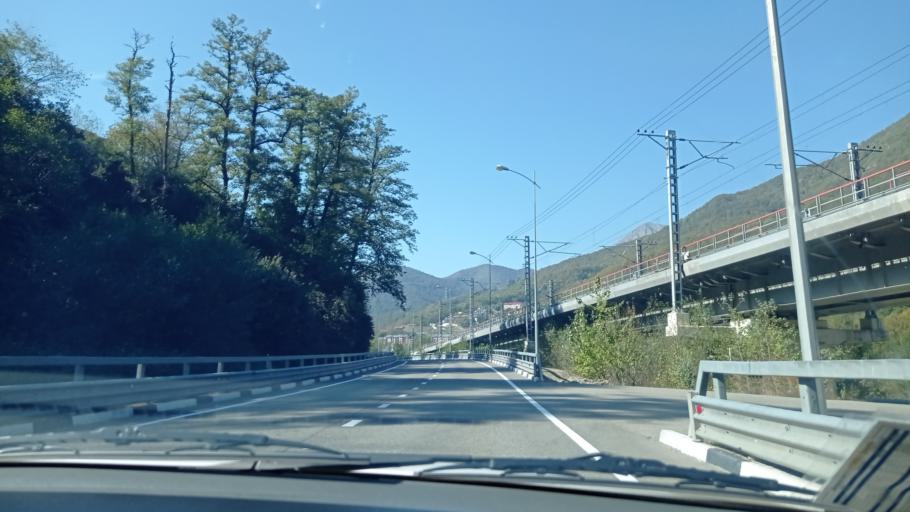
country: RU
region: Krasnodarskiy
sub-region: Sochi City
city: Krasnaya Polyana
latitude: 43.6837
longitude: 40.2396
